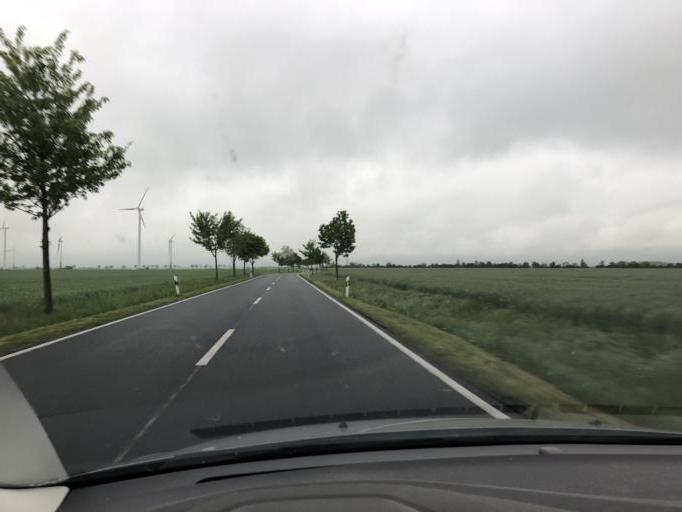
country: DE
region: Saxony
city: Dobernitz
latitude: 51.5086
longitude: 12.3758
